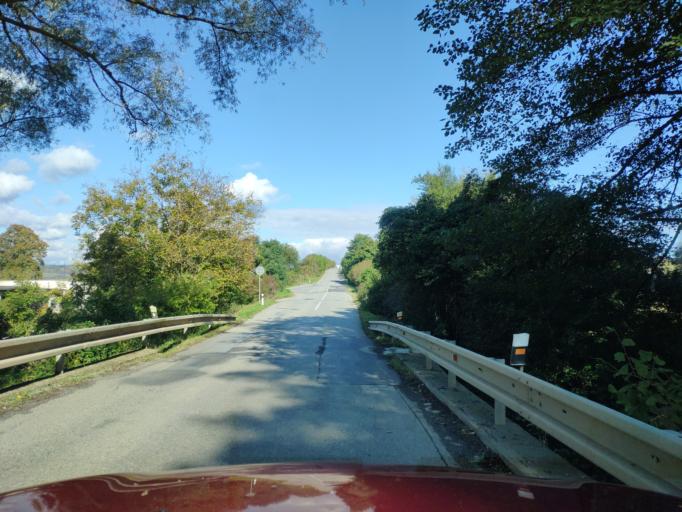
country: SK
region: Presovsky
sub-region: Okres Presov
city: Presov
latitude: 48.8895
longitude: 21.2607
